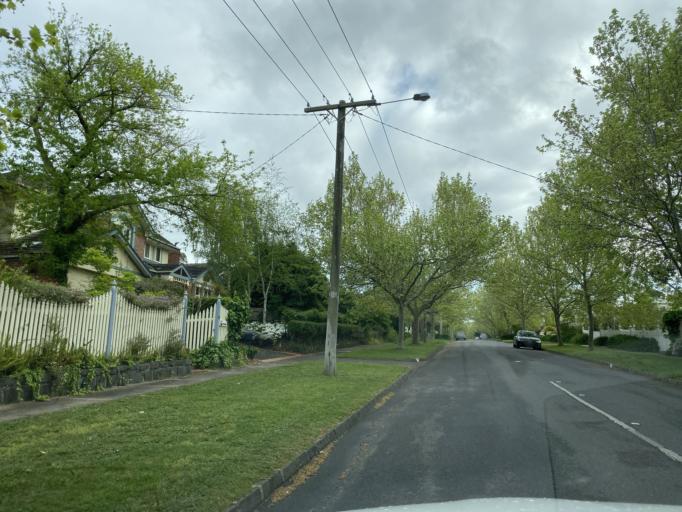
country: AU
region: Victoria
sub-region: Whitehorse
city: Surrey Hills
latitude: -37.8312
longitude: 145.0930
